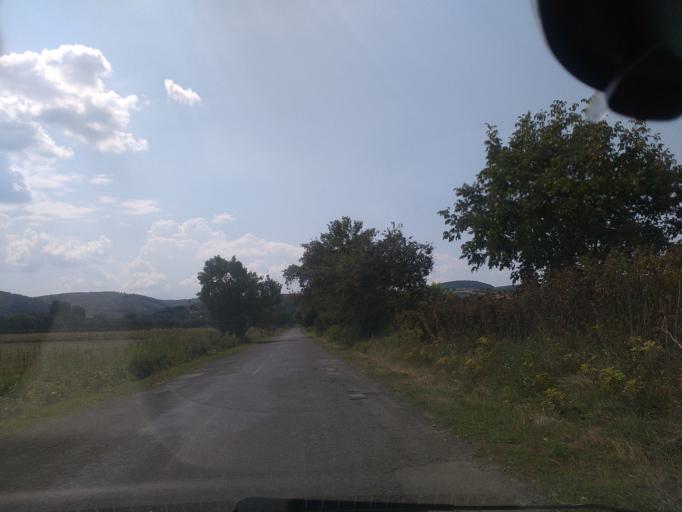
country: HU
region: Komarom-Esztergom
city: Pilismarot
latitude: 47.7926
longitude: 18.8806
